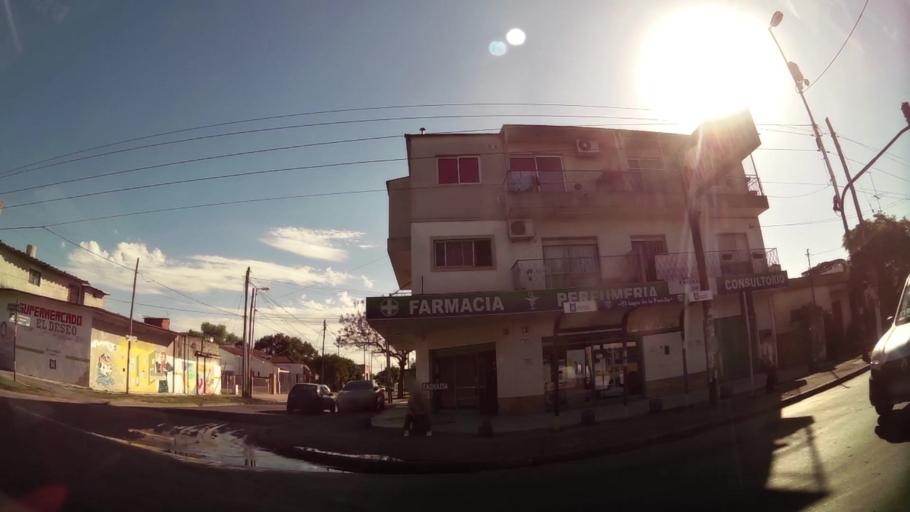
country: AR
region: Buenos Aires
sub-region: Partido de Tigre
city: Tigre
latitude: -34.4867
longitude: -58.6641
